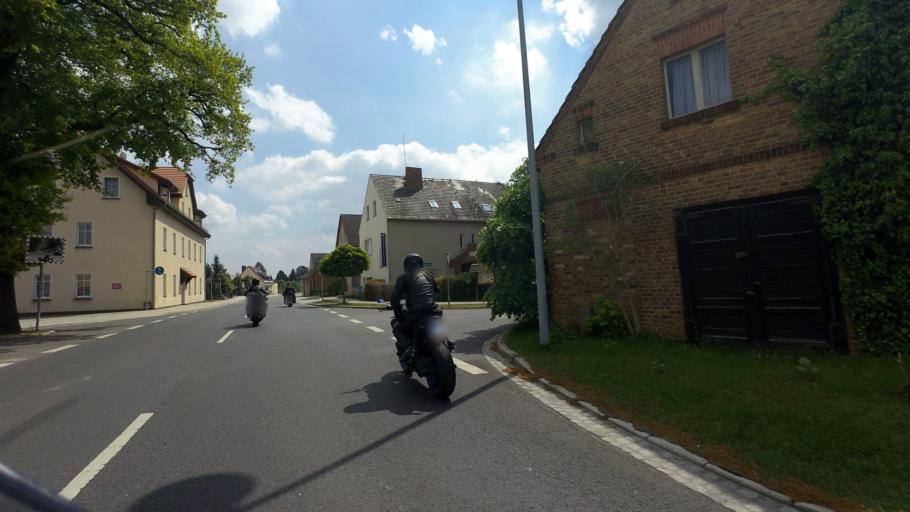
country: DE
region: Saxony
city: Weisskeissel
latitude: 51.4943
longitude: 14.7197
